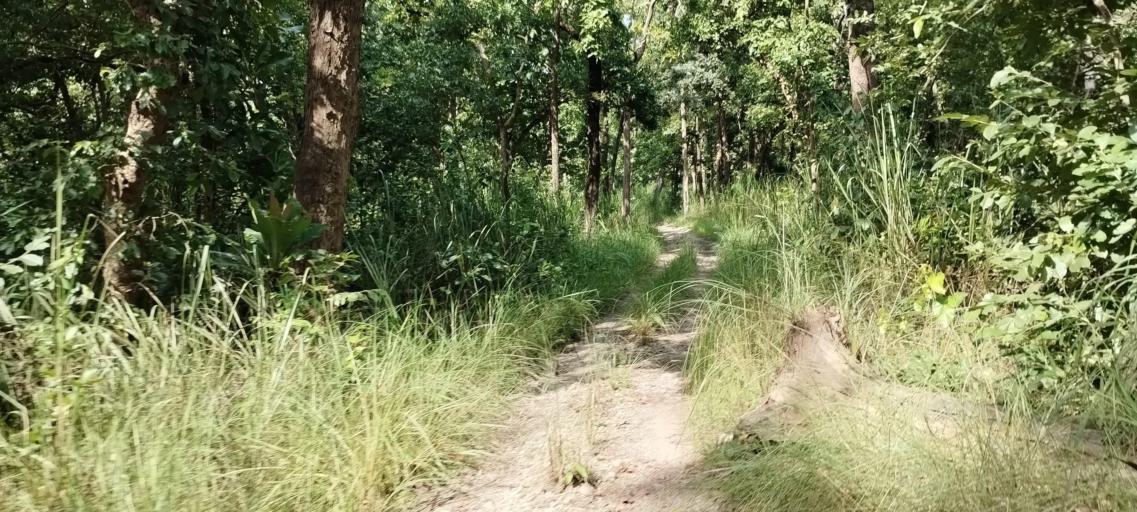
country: NP
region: Far Western
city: Tikapur
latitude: 28.5566
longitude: 81.2926
